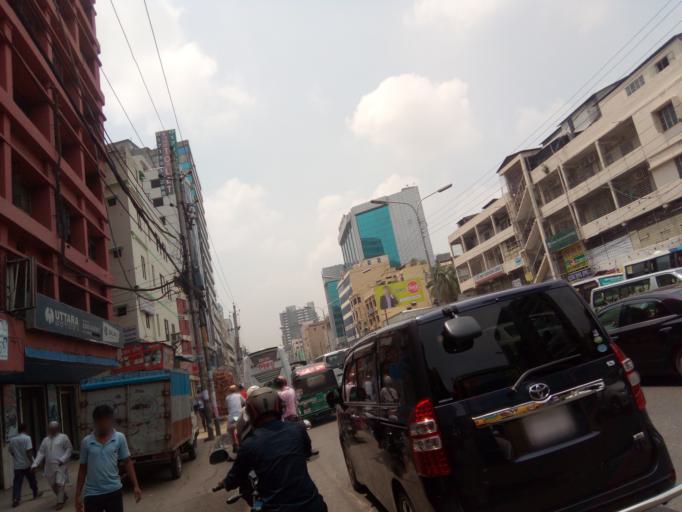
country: BD
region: Dhaka
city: Azimpur
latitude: 23.7555
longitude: 90.3912
